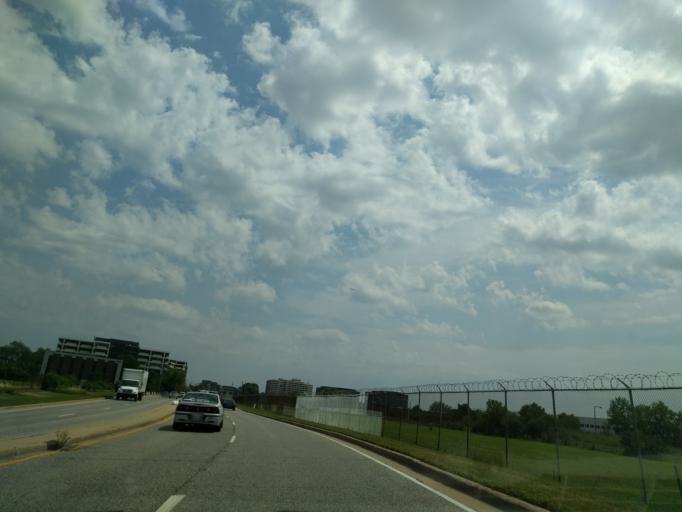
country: US
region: Illinois
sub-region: Cook County
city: Rosemont
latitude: 41.9997
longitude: -87.8935
